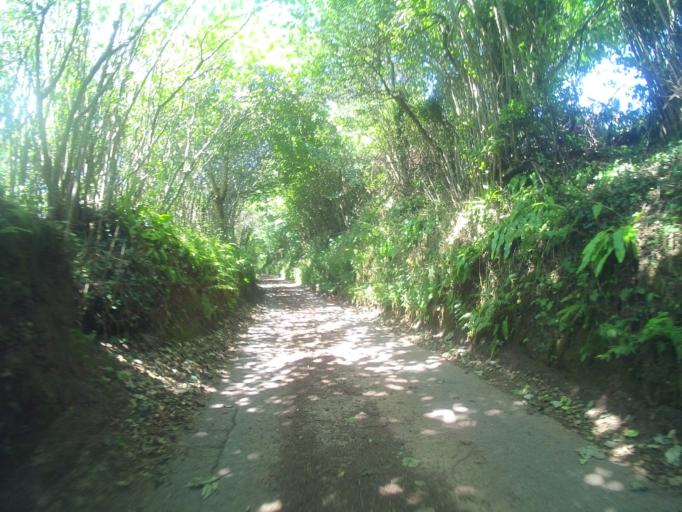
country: GB
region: England
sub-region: Devon
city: Dartmouth
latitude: 50.3618
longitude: -3.6193
